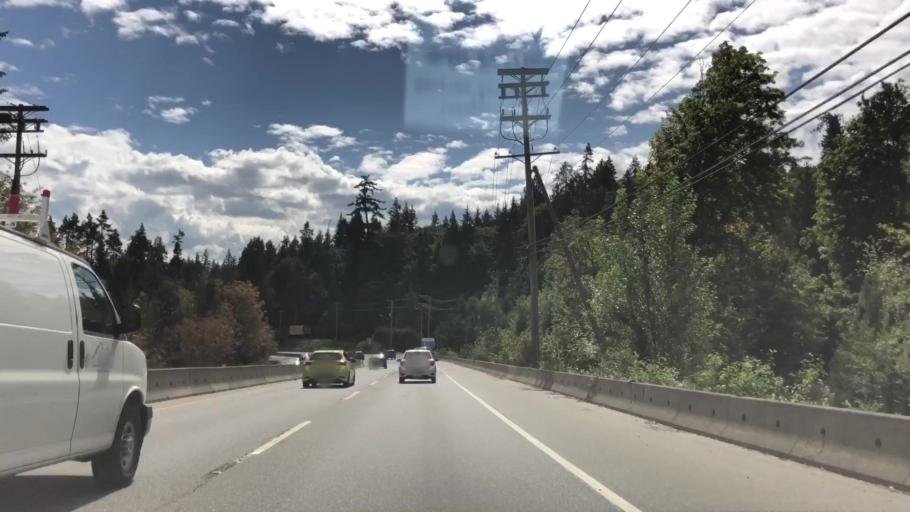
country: CA
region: British Columbia
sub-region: Cowichan Valley Regional District
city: Ladysmith
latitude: 49.0228
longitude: -123.8607
